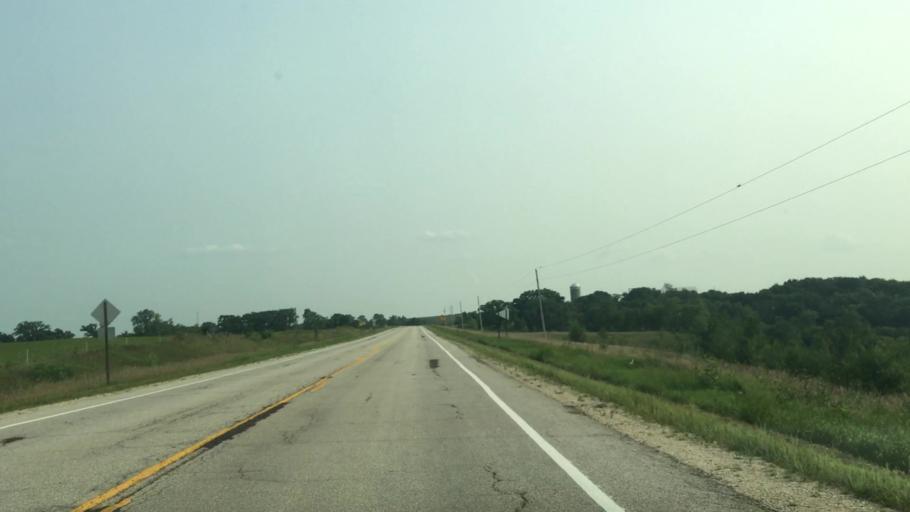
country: US
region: Minnesota
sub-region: Fillmore County
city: Preston
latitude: 43.6880
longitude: -91.9433
